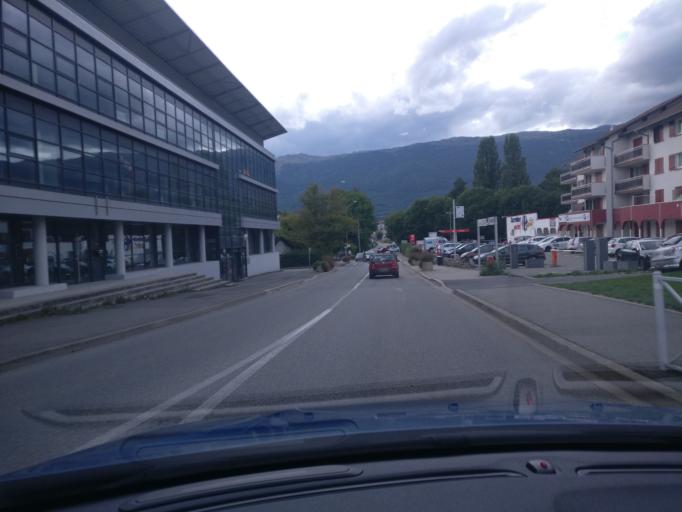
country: FR
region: Rhone-Alpes
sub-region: Departement de l'Ain
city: Saint-Genis-Pouilly
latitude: 46.2408
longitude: 6.0298
